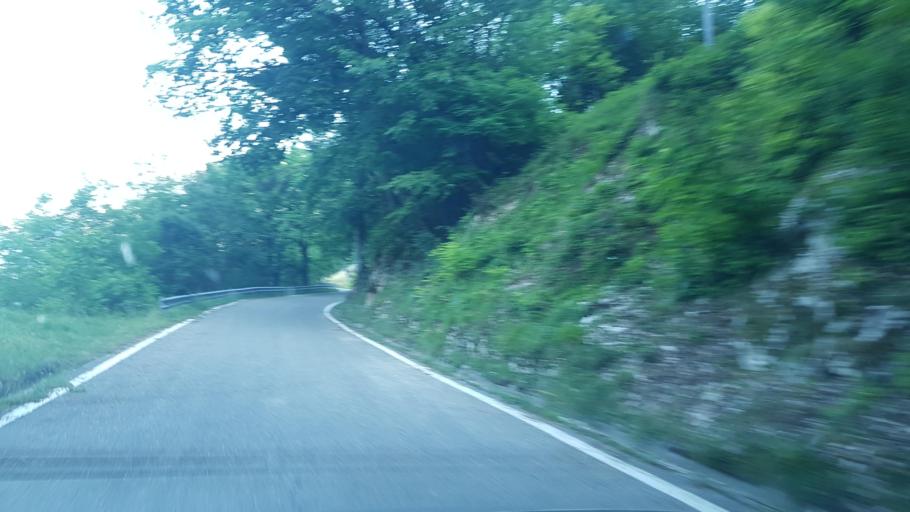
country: IT
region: Friuli Venezia Giulia
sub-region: Provincia di Udine
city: Dogna
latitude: 46.4522
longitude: 13.3598
